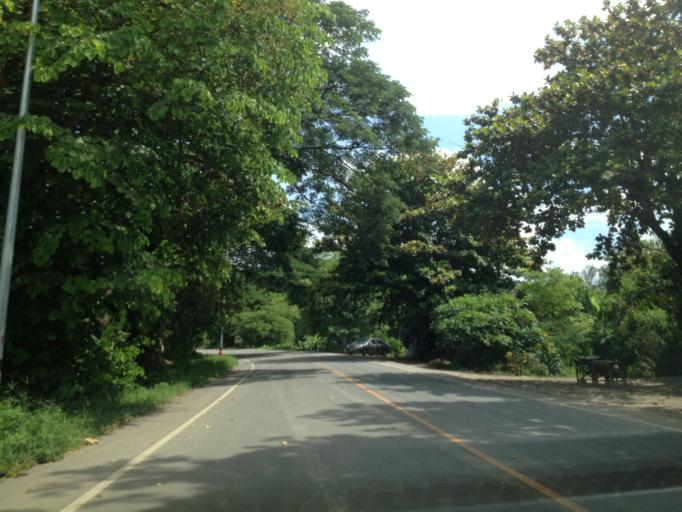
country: TH
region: Chiang Mai
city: Hang Dong
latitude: 18.7464
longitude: 98.8902
